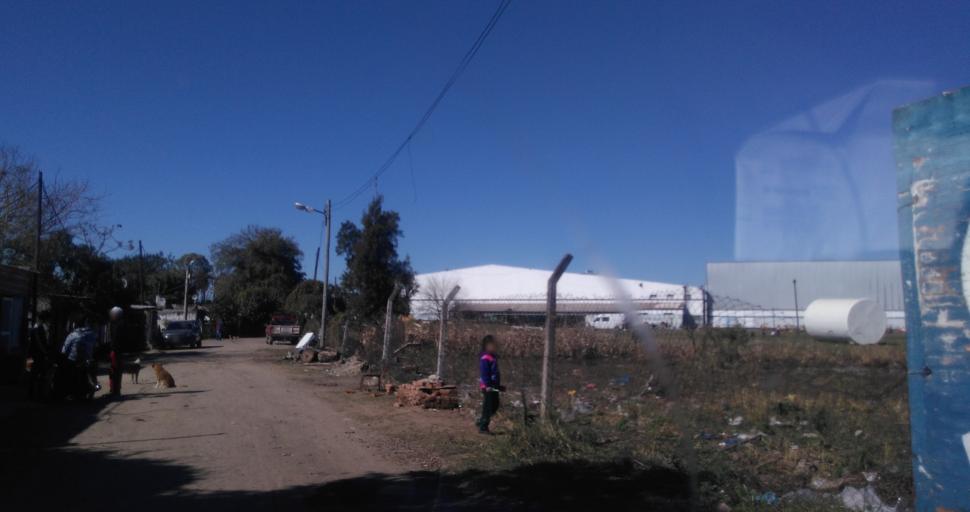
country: AR
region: Chaco
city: Fontana
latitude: -27.4270
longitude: -59.0127
